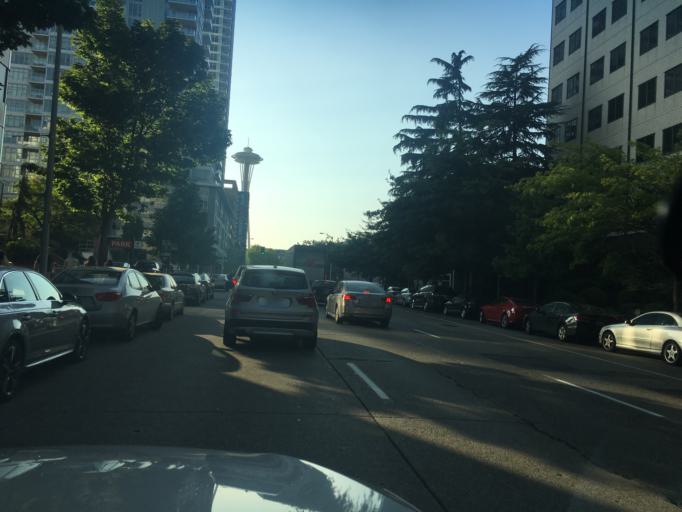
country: US
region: Washington
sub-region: King County
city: Seattle
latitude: 47.6161
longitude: -122.3413
